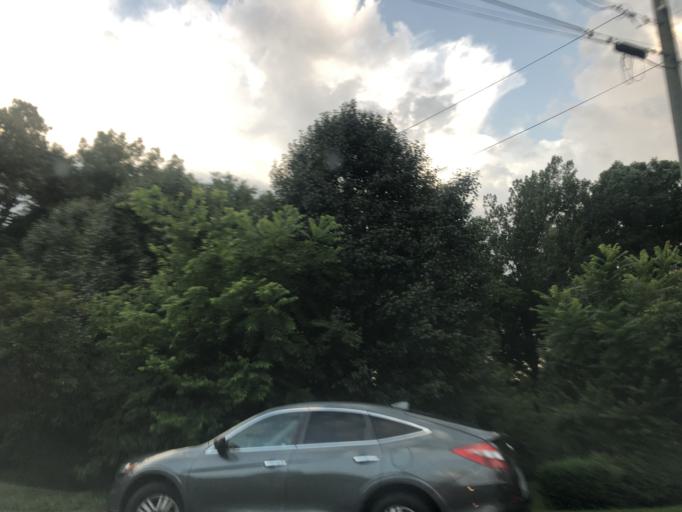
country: US
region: Tennessee
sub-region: Davidson County
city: Lakewood
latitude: 36.1438
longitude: -86.6361
